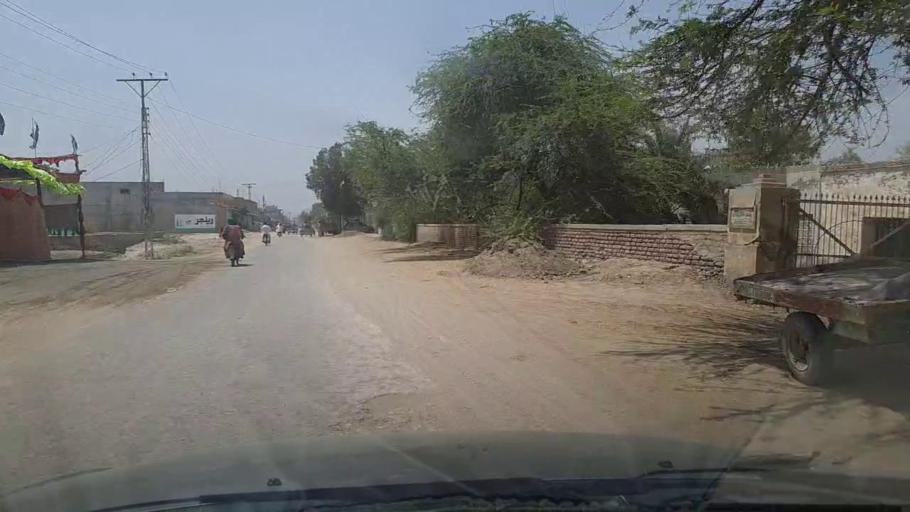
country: PK
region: Sindh
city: Bhiria
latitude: 26.8842
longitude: 68.2905
